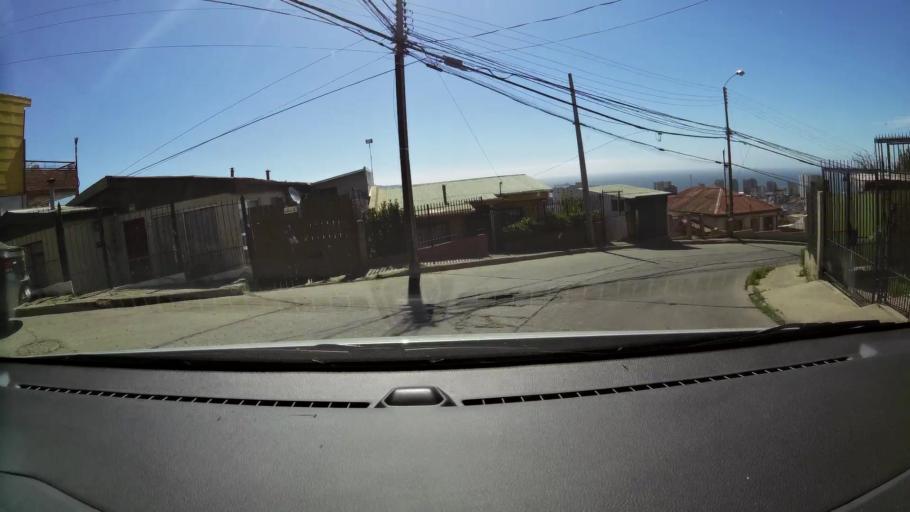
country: CL
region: Valparaiso
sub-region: Provincia de Valparaiso
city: Vina del Mar
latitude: -33.0369
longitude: -71.5737
